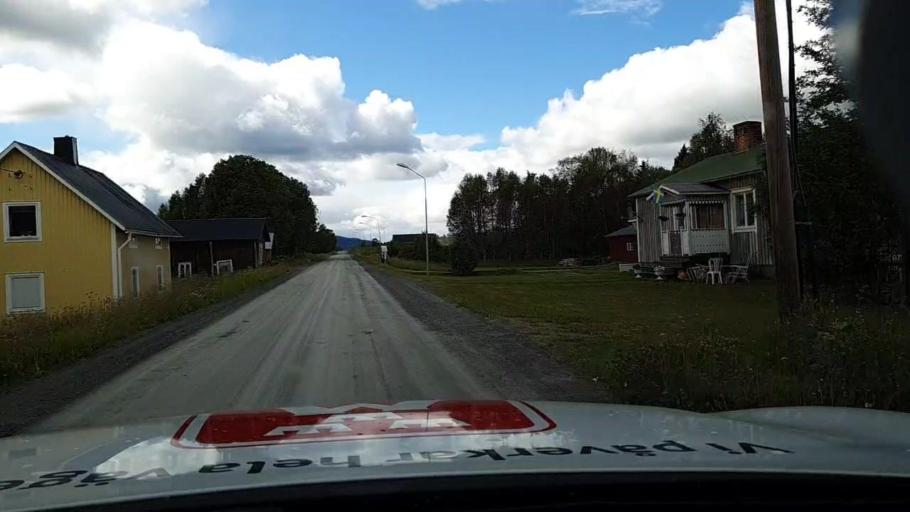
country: SE
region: Jaemtland
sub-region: Krokoms Kommun
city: Valla
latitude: 63.6947
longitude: 13.6482
